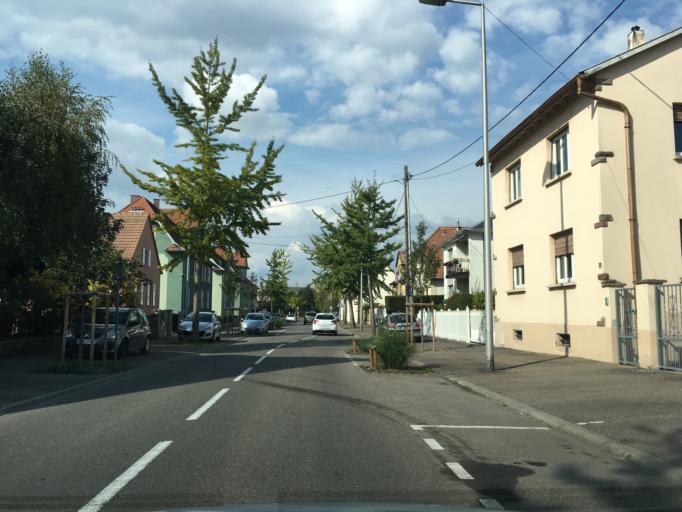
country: FR
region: Alsace
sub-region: Departement du Haut-Rhin
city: Horbourg-Wihr
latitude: 48.0788
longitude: 7.3822
